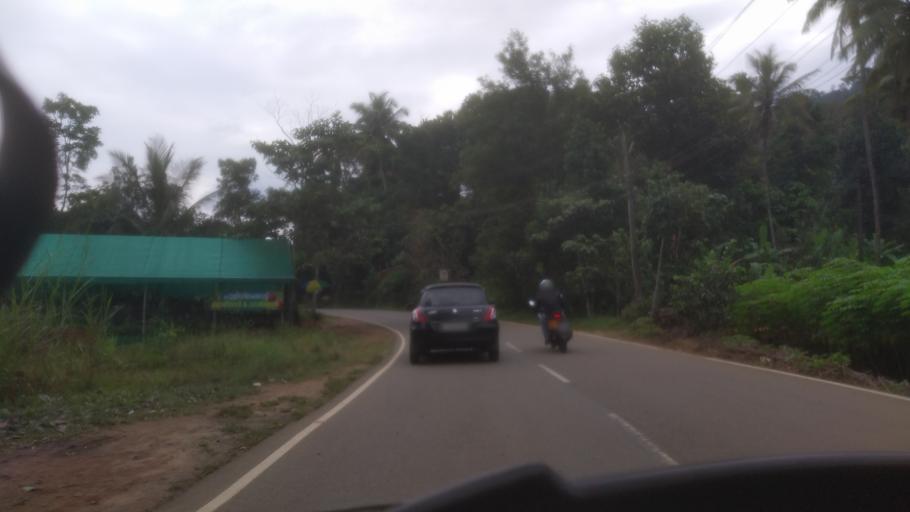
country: IN
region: Kerala
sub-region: Idukki
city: Munnar
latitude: 9.9891
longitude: 76.9840
